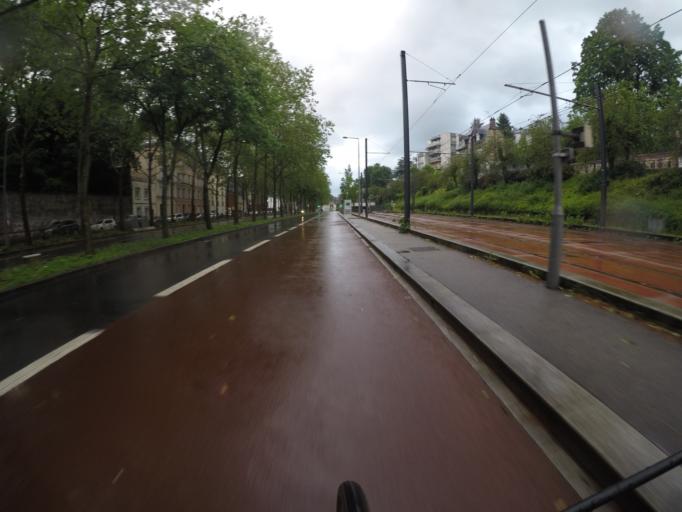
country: FR
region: Haute-Normandie
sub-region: Departement de la Seine-Maritime
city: Rouen
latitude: 49.4472
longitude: 1.1042
